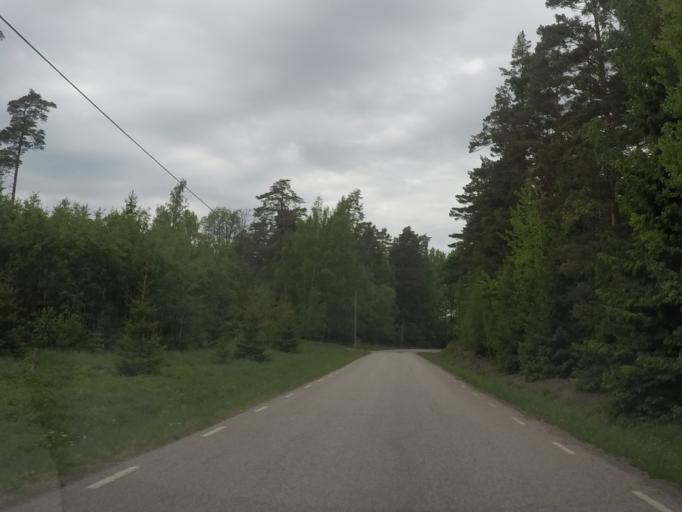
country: SE
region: Soedermanland
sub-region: Nykopings Kommun
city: Stigtomta
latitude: 58.9120
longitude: 16.8814
